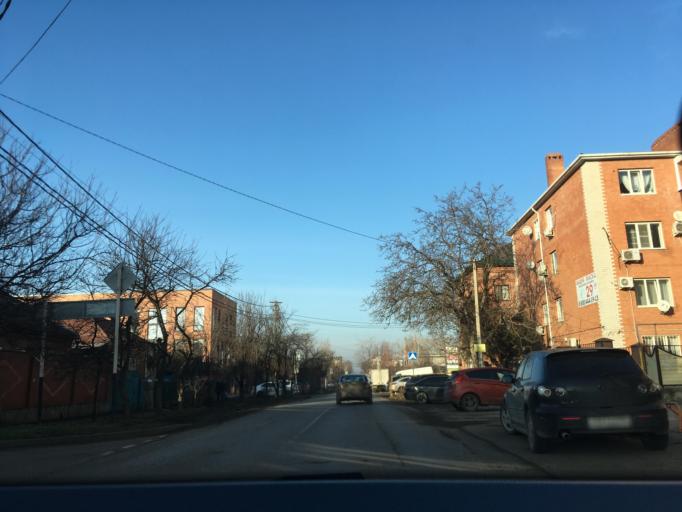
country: RU
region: Krasnodarskiy
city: Krasnodar
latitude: 45.0687
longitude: 39.0216
